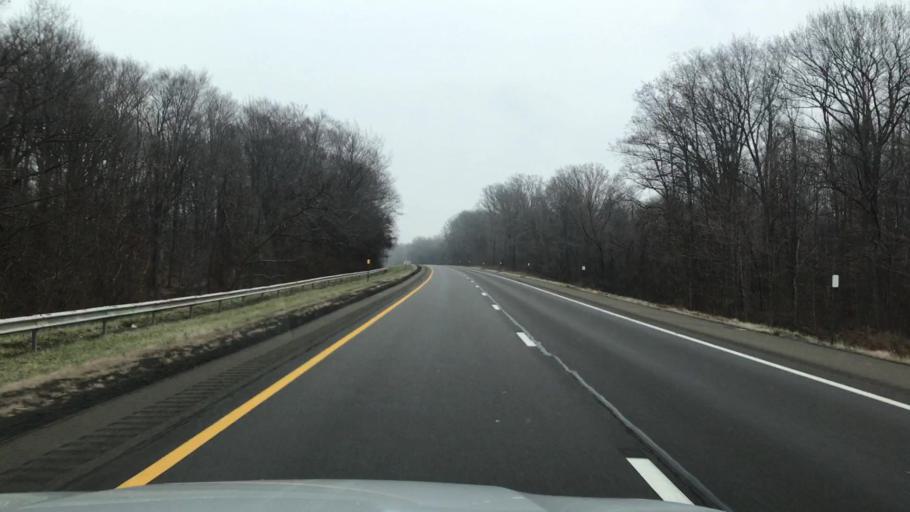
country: US
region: New York
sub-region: Chautauqua County
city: Brocton
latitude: 42.3793
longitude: -79.4954
